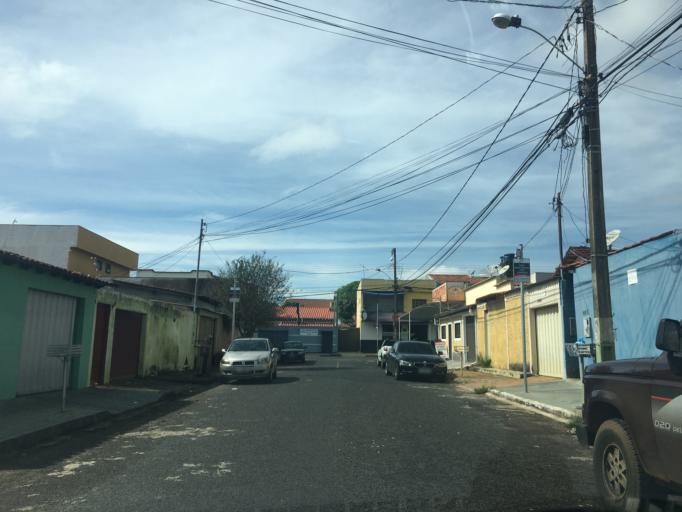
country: BR
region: Minas Gerais
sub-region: Uberlandia
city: Uberlandia
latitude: -18.9378
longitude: -48.3161
